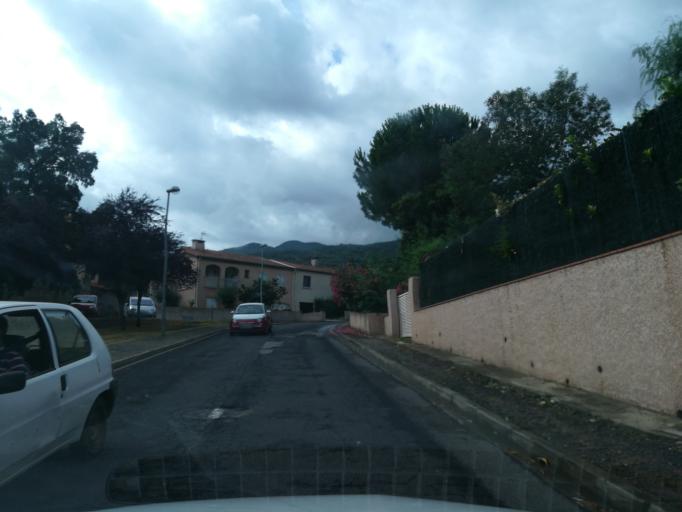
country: FR
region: Languedoc-Roussillon
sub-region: Departement des Pyrenees-Orientales
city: Ceret
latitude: 42.4871
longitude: 2.7447
